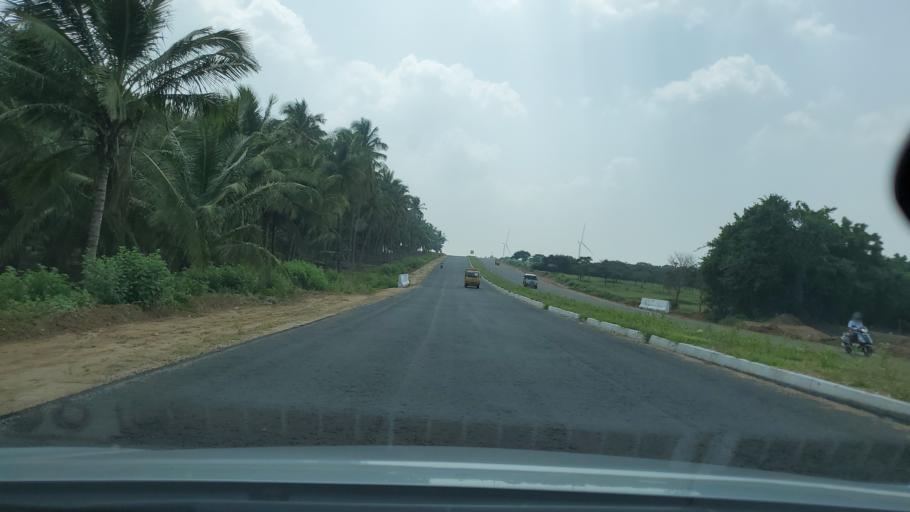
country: IN
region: Tamil Nadu
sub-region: Tiruppur
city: Dharapuram
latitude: 10.8803
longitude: 77.4624
